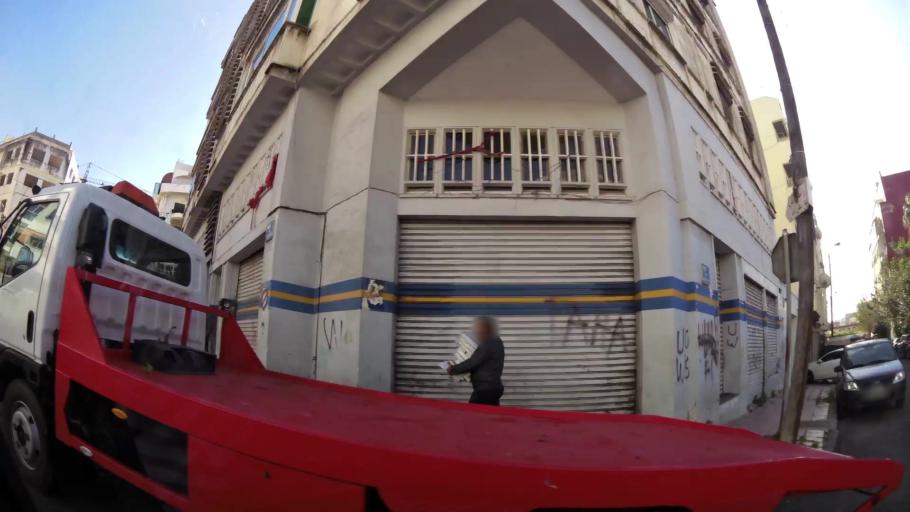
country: MA
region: Grand Casablanca
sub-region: Casablanca
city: Casablanca
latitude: 33.5937
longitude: -7.5894
